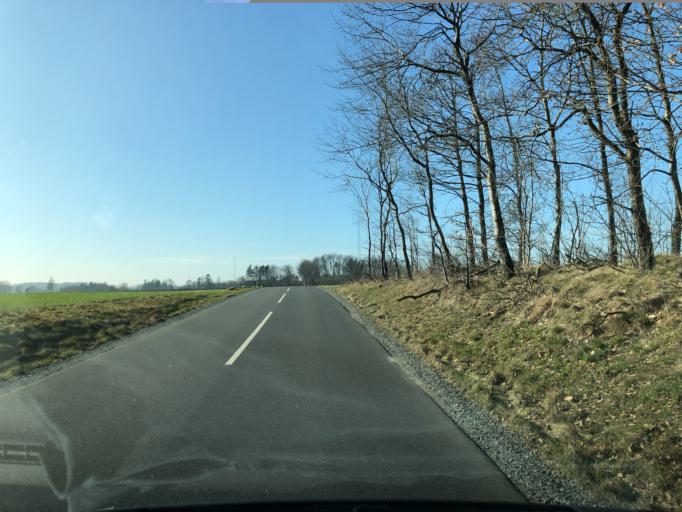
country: DK
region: Central Jutland
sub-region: Ikast-Brande Kommune
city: Bording Kirkeby
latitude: 56.1636
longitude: 9.3399
